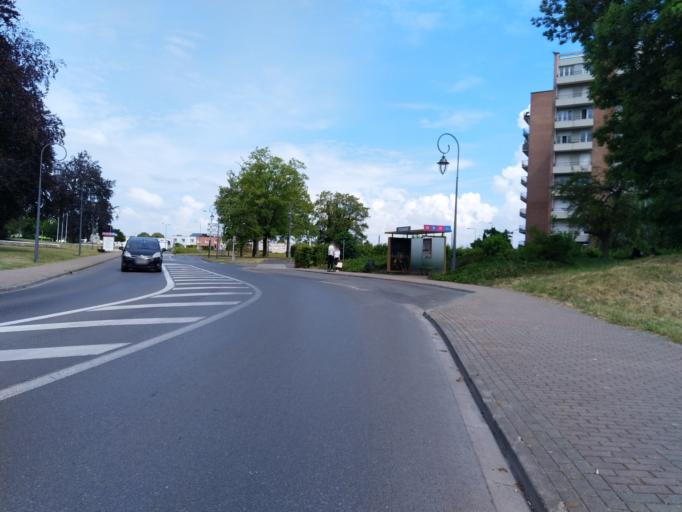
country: FR
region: Nord-Pas-de-Calais
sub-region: Departement du Nord
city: Maubeuge
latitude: 50.2814
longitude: 3.9759
